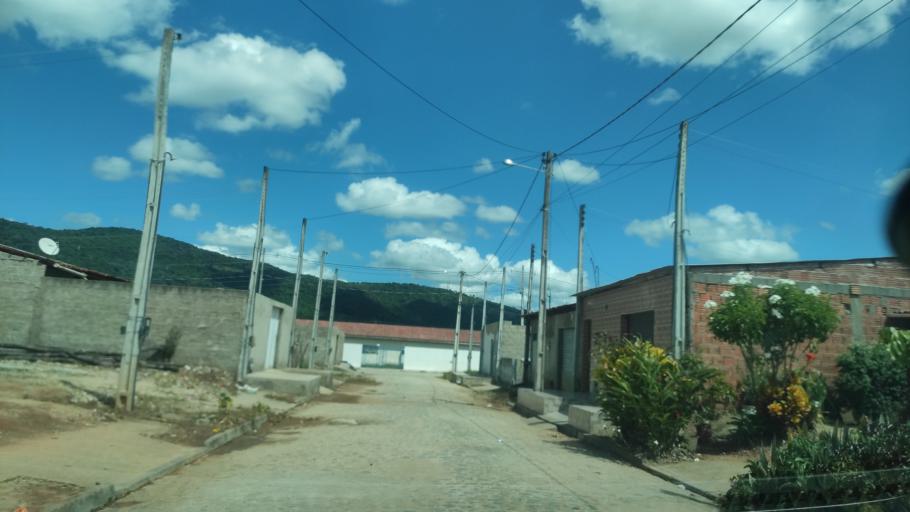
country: BR
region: Alagoas
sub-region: Uniao Dos Palmares
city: Uniao dos Palmares
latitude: -9.1449
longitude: -36.0023
